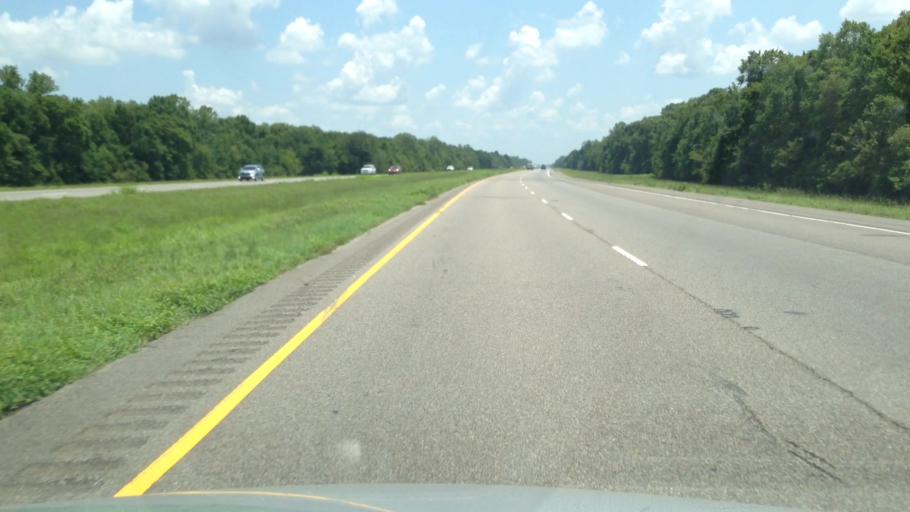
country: US
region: Louisiana
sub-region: Avoyelles Parish
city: Bunkie
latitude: 30.9831
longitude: -92.3023
